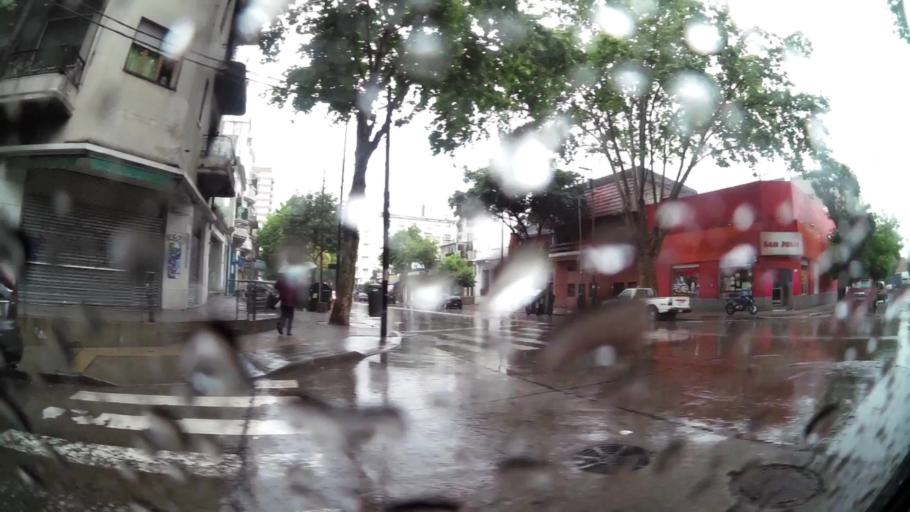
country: AR
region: Buenos Aires
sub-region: Partido de Avellaneda
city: Avellaneda
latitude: -34.6439
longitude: -58.3687
